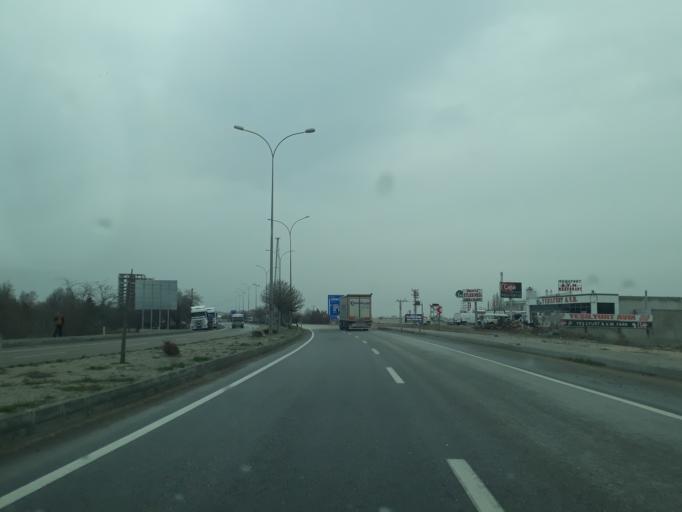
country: TR
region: Konya
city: Karapinar
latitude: 37.7154
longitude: 33.5777
